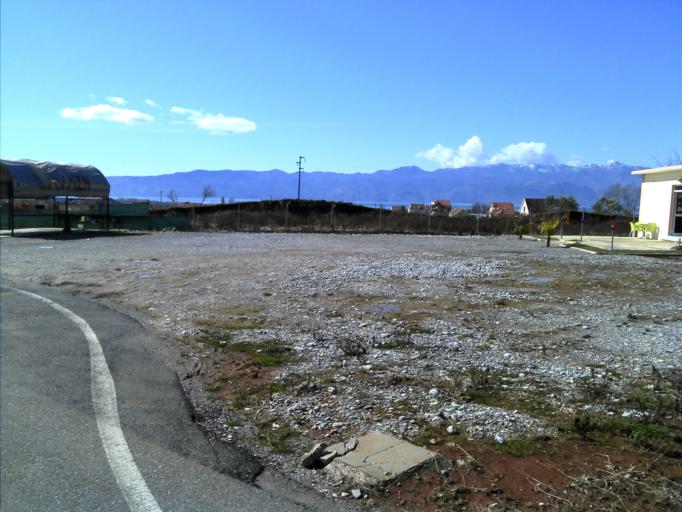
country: AL
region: Shkoder
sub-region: Rrethi i Malesia e Madhe
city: Koplik
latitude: 42.1971
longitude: 19.4555
